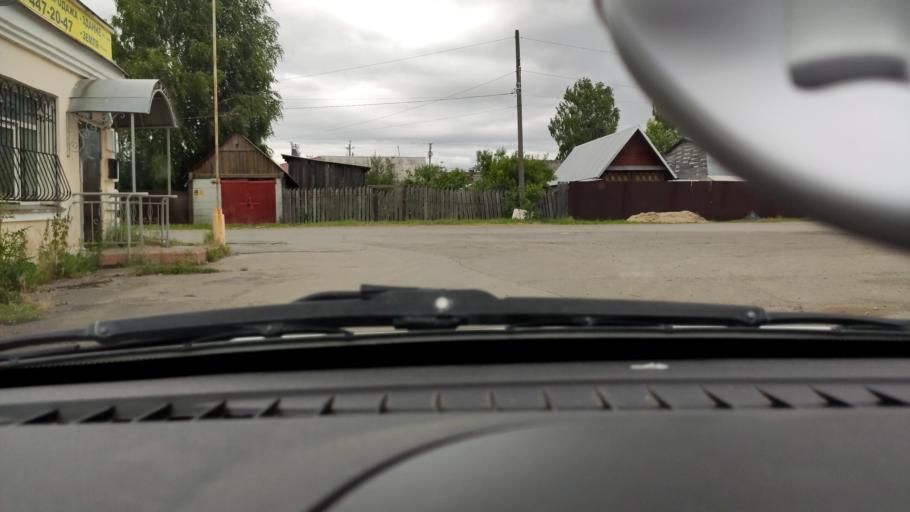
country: RU
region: Perm
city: Ferma
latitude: 57.8931
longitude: 56.2966
